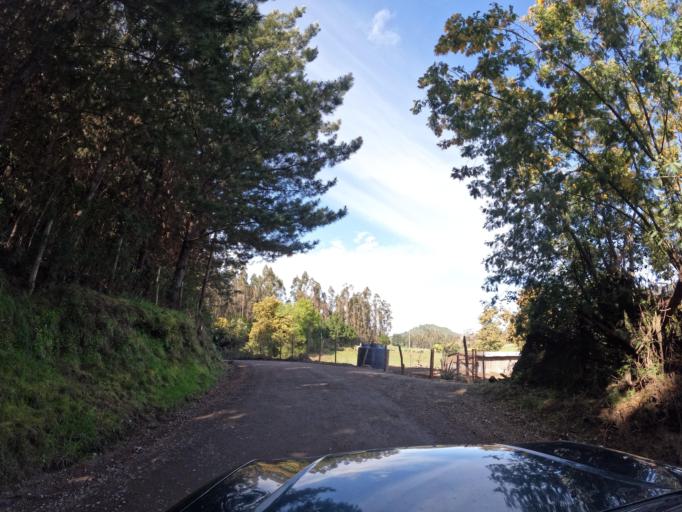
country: CL
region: Biobio
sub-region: Provincia de Concepcion
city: Chiguayante
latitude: -37.0629
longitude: -72.8966
